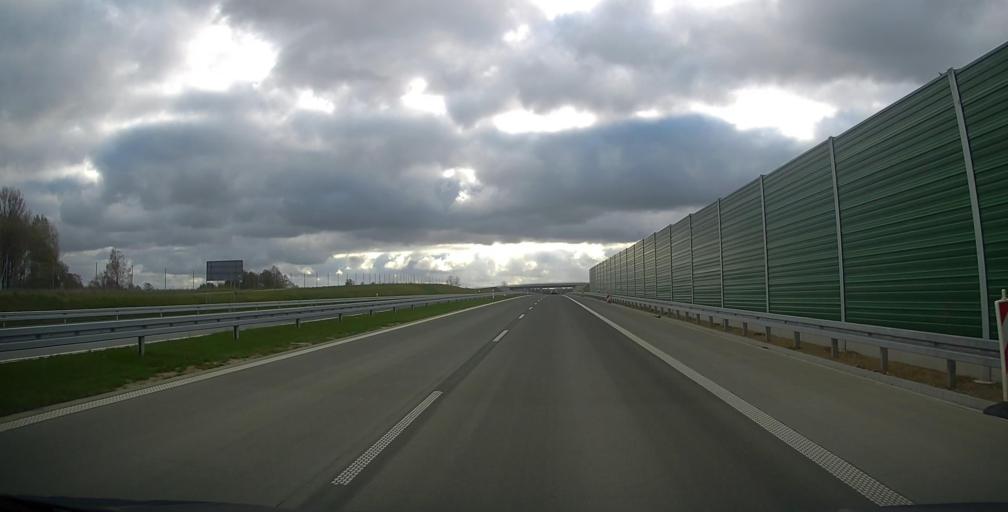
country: PL
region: Podlasie
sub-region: Powiat suwalski
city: Raczki
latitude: 53.9456
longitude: 22.7652
